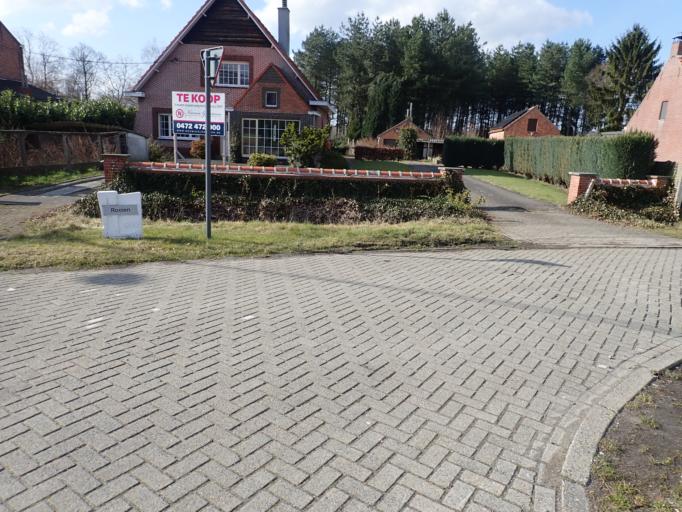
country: BE
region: Flanders
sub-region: Provincie Antwerpen
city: Vosselaar
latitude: 51.2775
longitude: 4.8857
